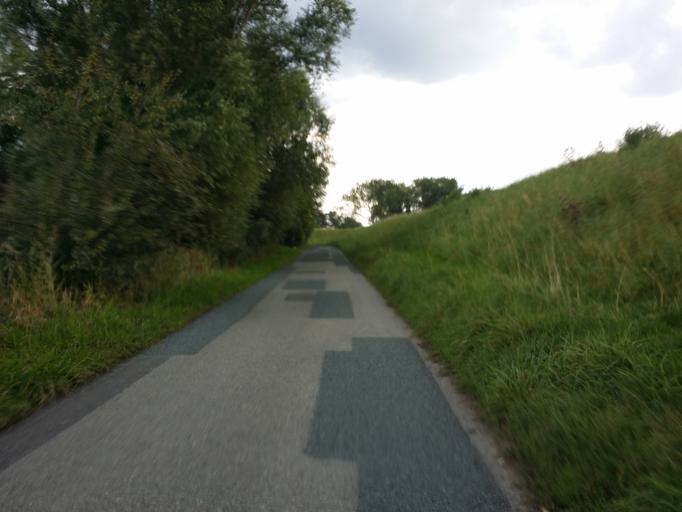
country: DE
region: Lower Saxony
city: Hemmoor
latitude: 53.7087
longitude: 9.1609
